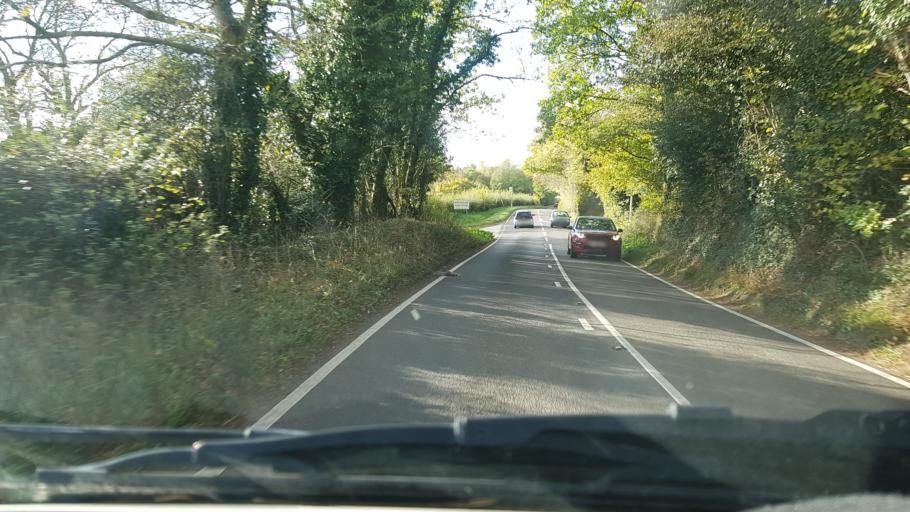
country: GB
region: England
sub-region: Surrey
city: East Horsley
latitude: 51.2145
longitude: -0.4243
